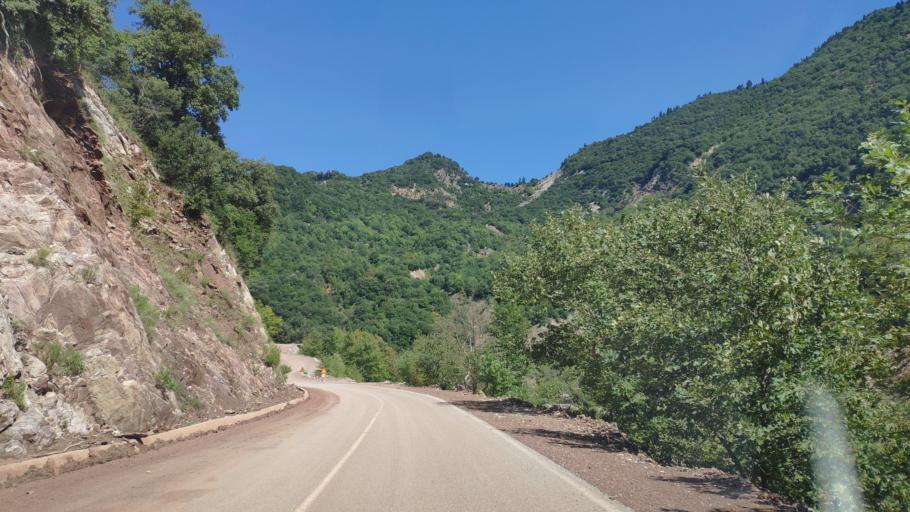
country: GR
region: Central Greece
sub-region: Nomos Evrytanias
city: Kerasochori
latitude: 39.0675
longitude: 21.6065
